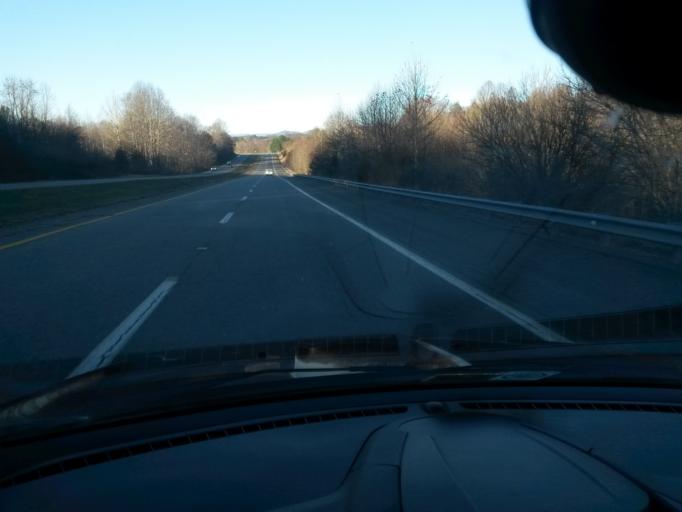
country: US
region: Virginia
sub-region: Henry County
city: Horse Pasture
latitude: 36.6221
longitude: -79.9871
